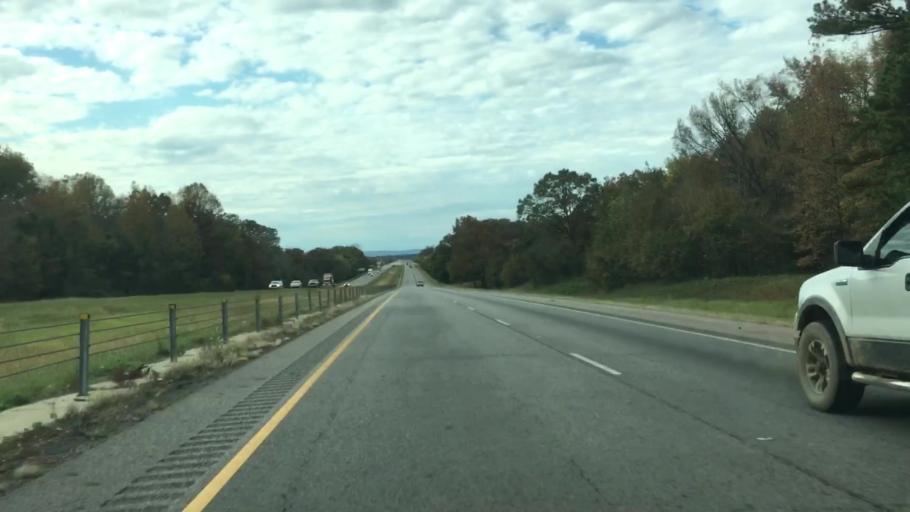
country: US
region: Arkansas
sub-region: Conway County
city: Morrilton
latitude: 35.1811
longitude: -92.7607
